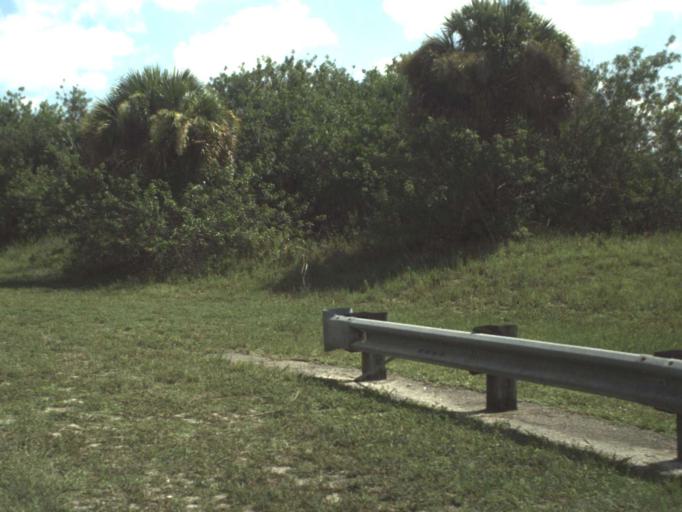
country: US
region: Florida
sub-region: Saint Lucie County
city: Port Saint Lucie
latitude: 27.2174
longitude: -80.3719
